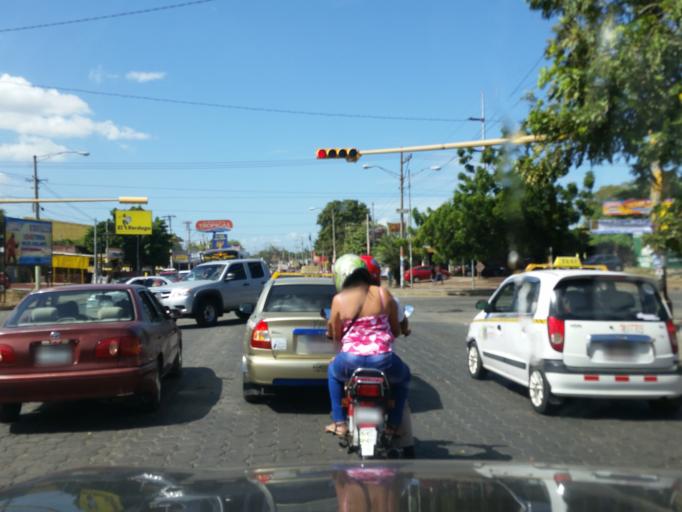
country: NI
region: Managua
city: Managua
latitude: 12.1284
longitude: -86.2172
